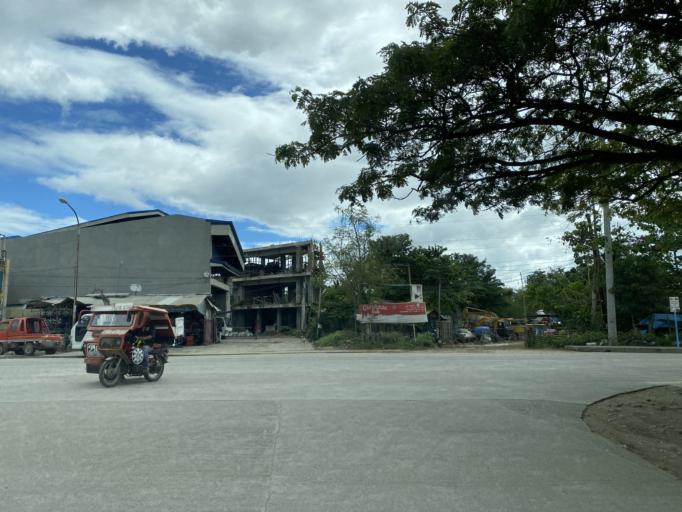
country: PH
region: Central Visayas
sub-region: Province of Bohol
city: Tagbilaran City
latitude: 9.6560
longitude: 123.8724
